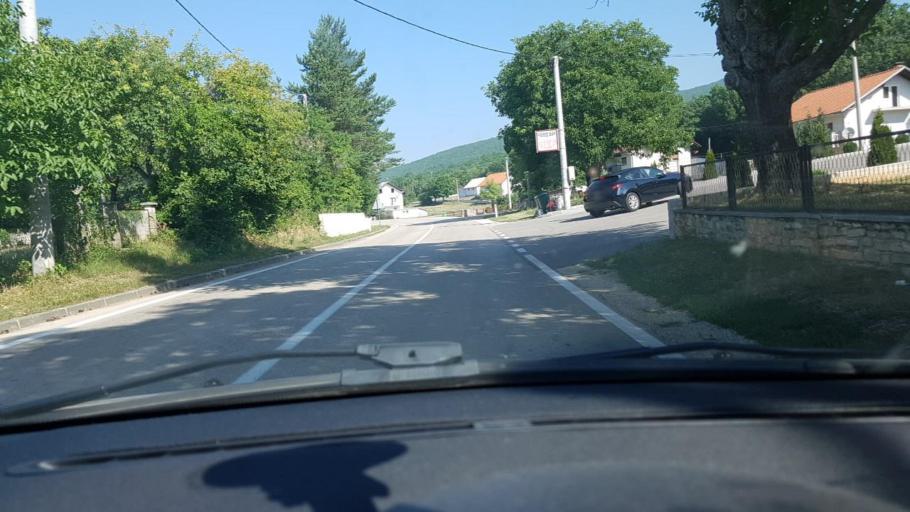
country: BA
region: Federation of Bosnia and Herzegovina
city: Orguz
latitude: 43.8702
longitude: 16.8763
